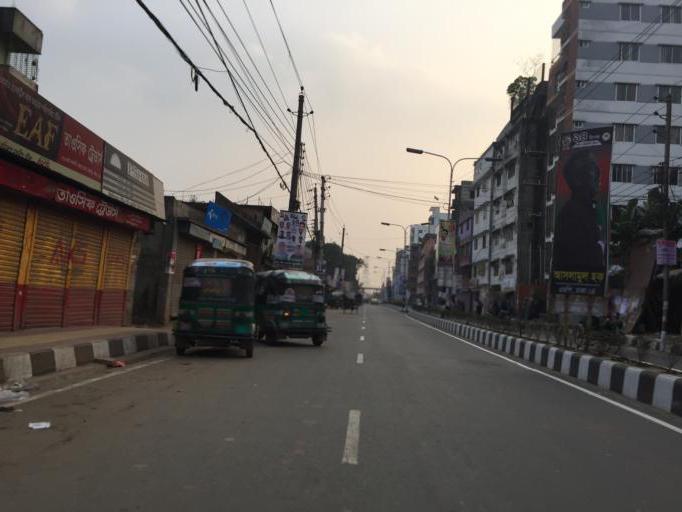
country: BD
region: Dhaka
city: Azimpur
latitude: 23.7864
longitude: 90.3478
